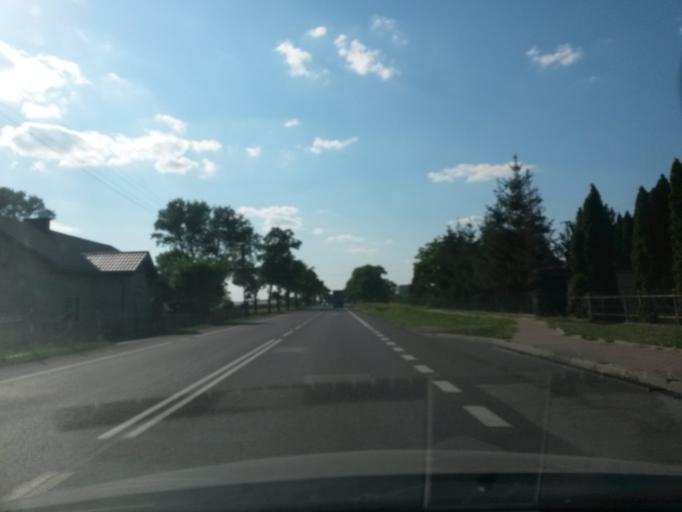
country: PL
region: Masovian Voivodeship
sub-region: Powiat sierpecki
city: Zawidz
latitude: 52.8106
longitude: 19.8180
